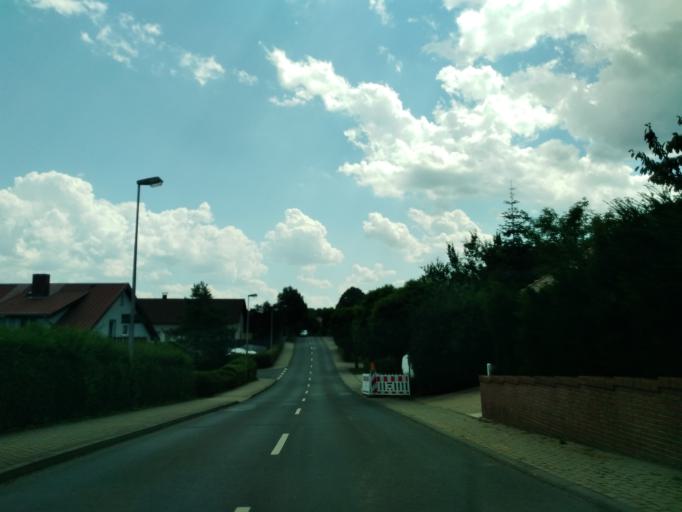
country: DE
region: Baden-Wuerttemberg
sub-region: Karlsruhe Region
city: Buchen
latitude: 49.5186
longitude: 9.3120
